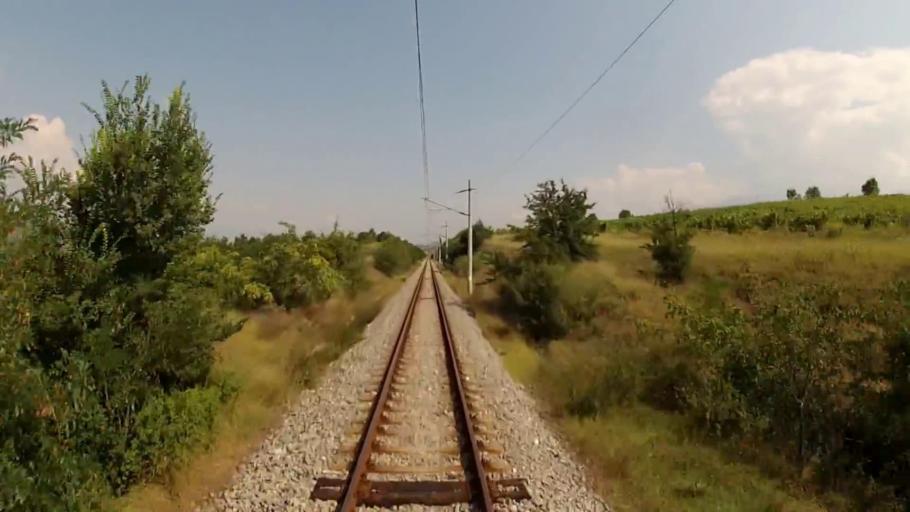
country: BG
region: Blagoevgrad
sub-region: Obshtina Sandanski
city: Sandanski
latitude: 41.5789
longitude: 23.2399
